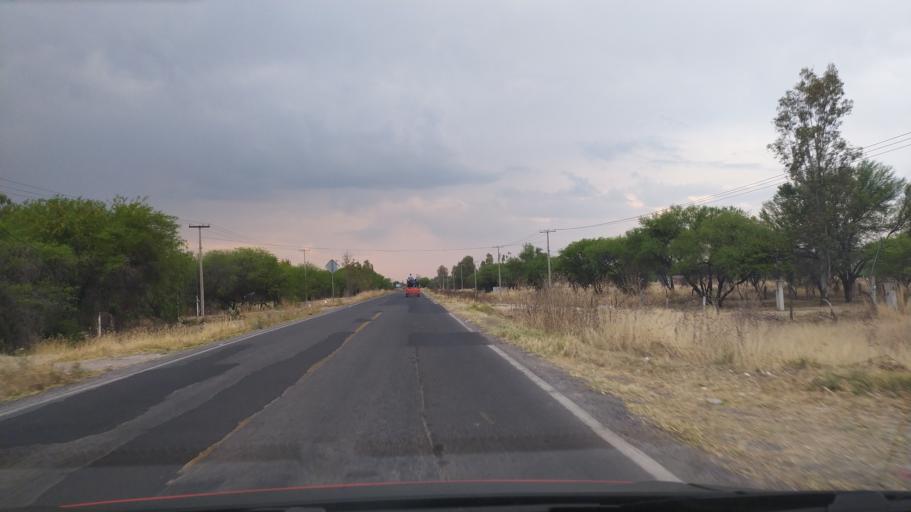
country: MX
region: Guanajuato
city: Ciudad Manuel Doblado
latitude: 20.7941
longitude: -101.9061
